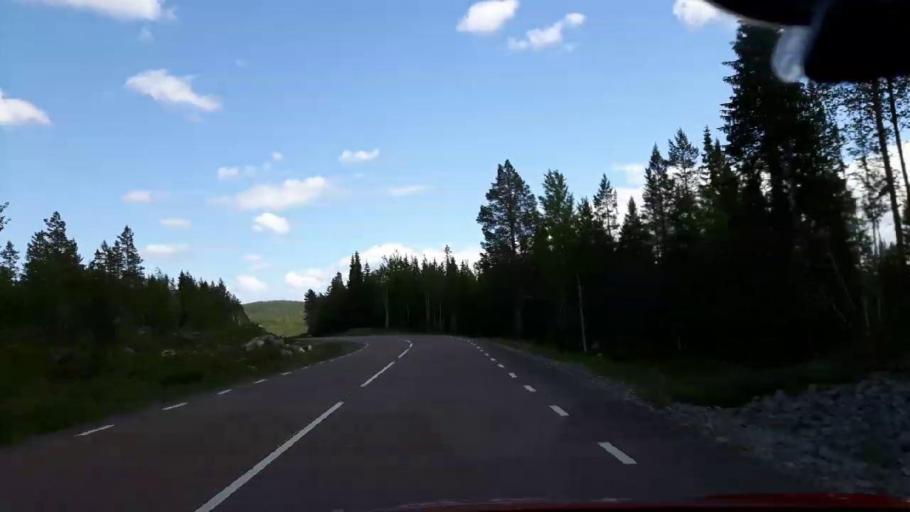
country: SE
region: Jaemtland
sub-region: Krokoms Kommun
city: Valla
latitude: 64.0467
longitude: 14.1789
